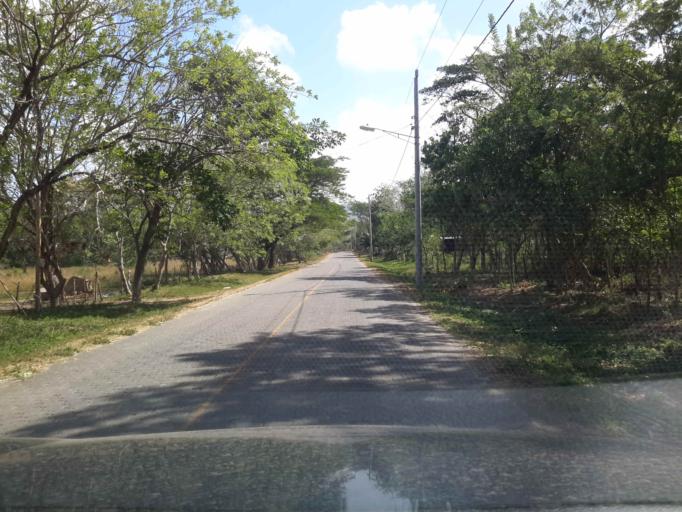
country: NI
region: Rivas
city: San Juan del Sur
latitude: 11.2450
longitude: -85.8405
